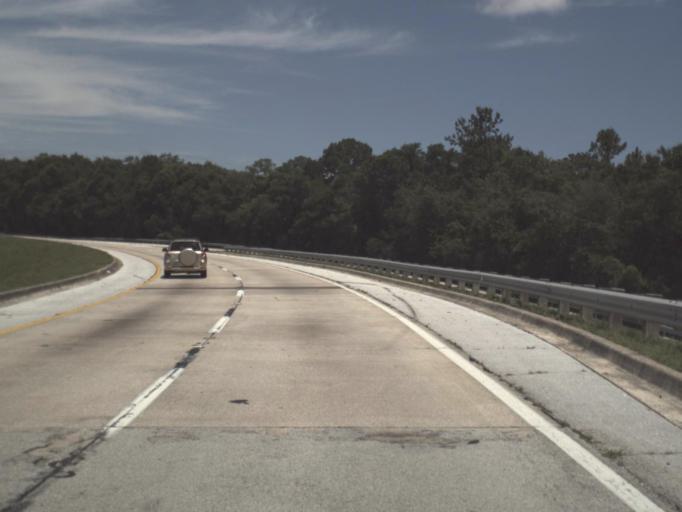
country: US
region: Florida
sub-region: Duval County
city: Jacksonville
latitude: 30.3030
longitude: -81.6123
